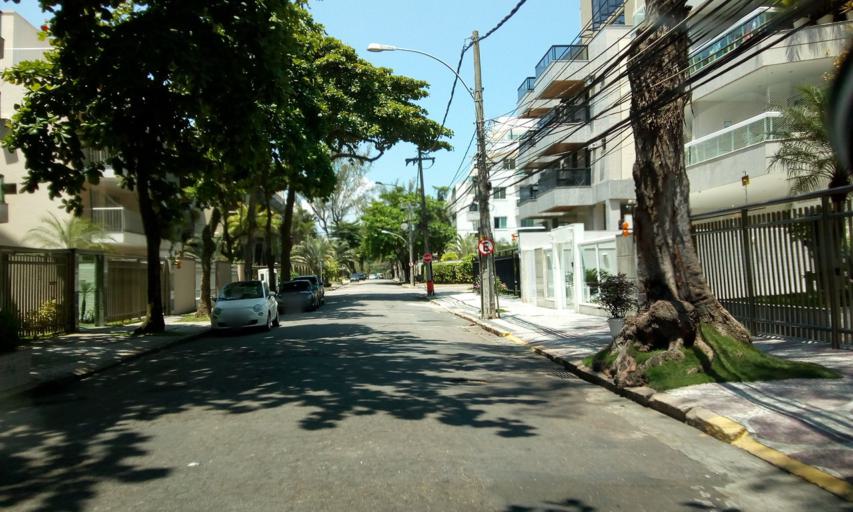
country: BR
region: Rio de Janeiro
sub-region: Nilopolis
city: Nilopolis
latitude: -23.0257
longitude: -43.4647
